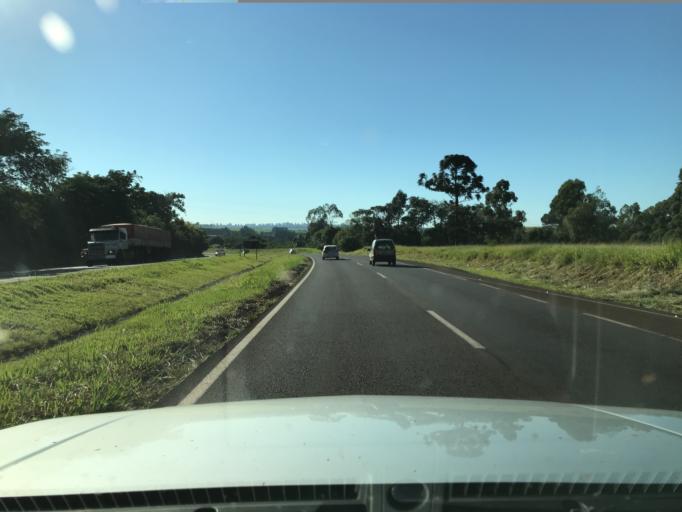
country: BR
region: Parana
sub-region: Cascavel
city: Cascavel
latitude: -24.8916
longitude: -53.5502
